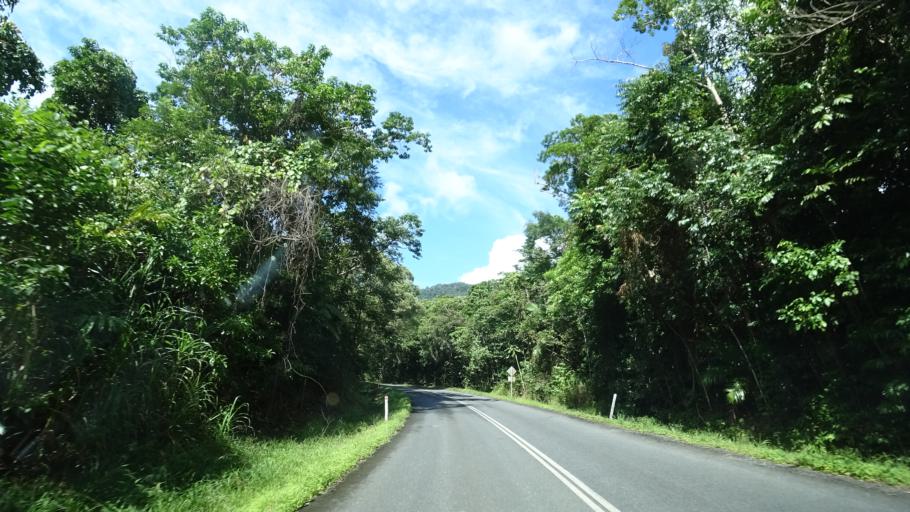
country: AU
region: Queensland
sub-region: Cairns
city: Port Douglas
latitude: -16.1408
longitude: 145.4305
